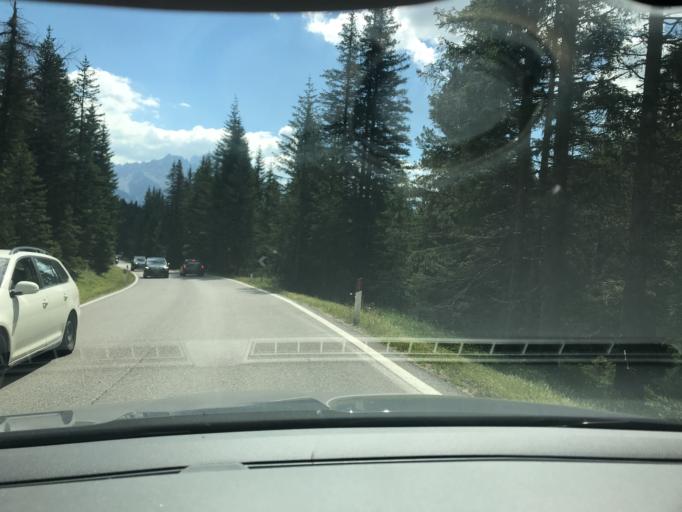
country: IT
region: Veneto
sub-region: Provincia di Belluno
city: Selva di Cadore
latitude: 46.5224
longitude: 12.0613
